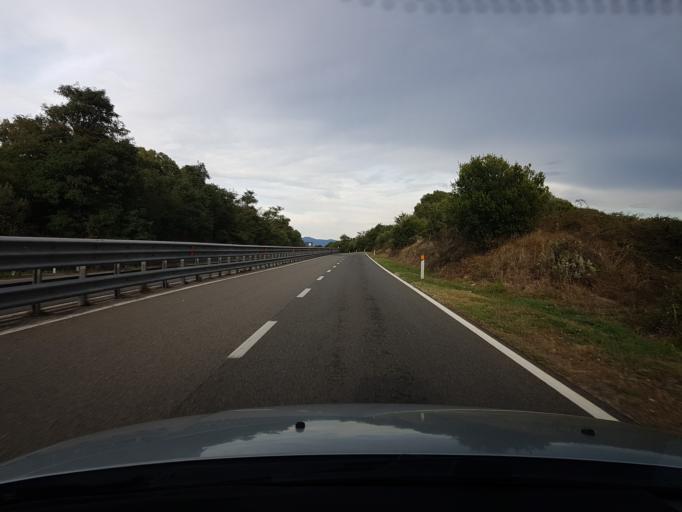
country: IT
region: Sardinia
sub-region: Provincia di Oristano
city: Soddi
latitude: 40.1488
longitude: 8.8903
